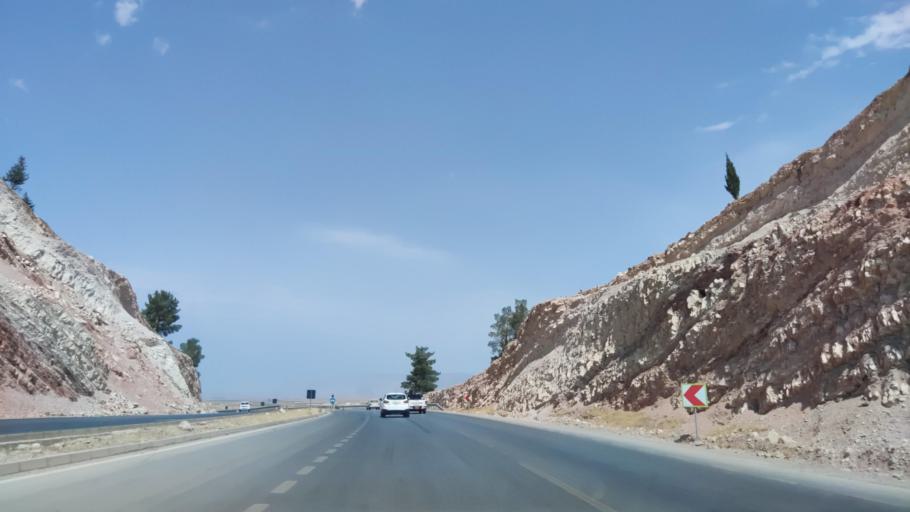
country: IQ
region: Arbil
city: Shaqlawah
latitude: 36.4882
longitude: 44.3801
